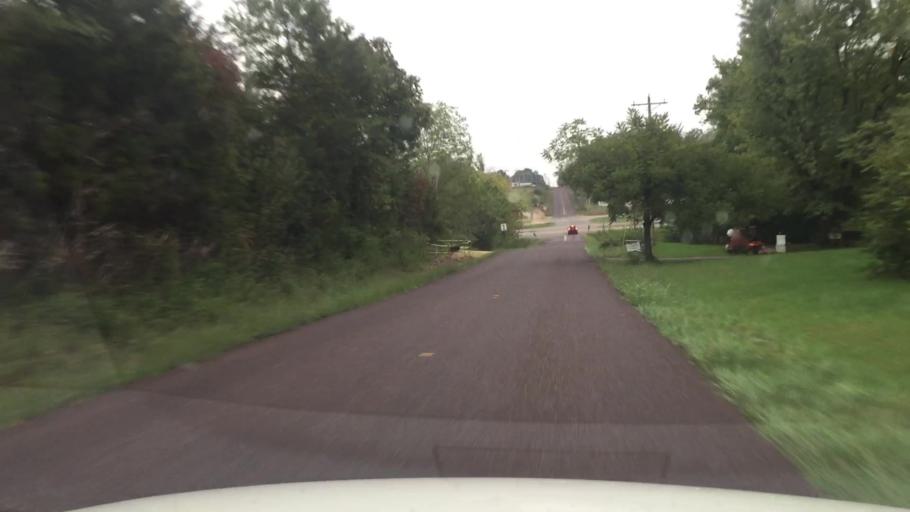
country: US
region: Missouri
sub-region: Boone County
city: Ashland
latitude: 38.8106
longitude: -92.2537
